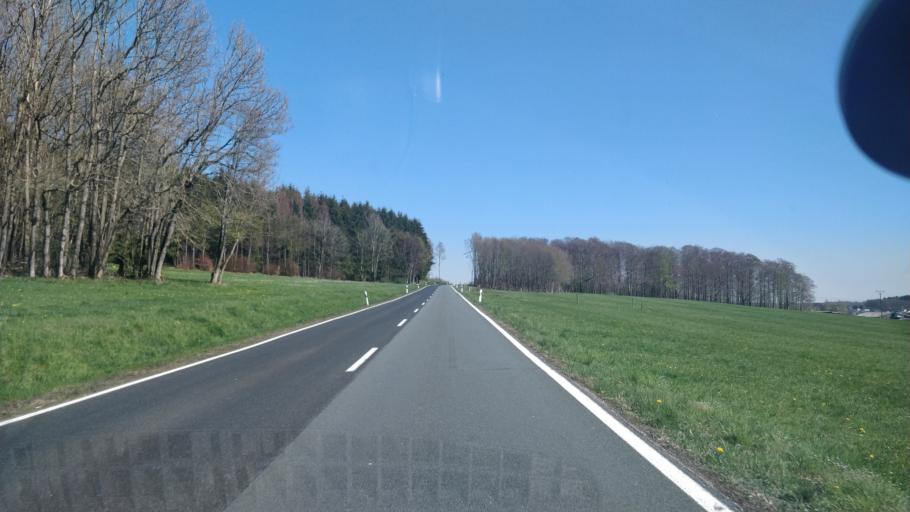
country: DE
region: Rheinland-Pfalz
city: Niederrossbach
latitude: 50.6411
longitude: 8.0193
